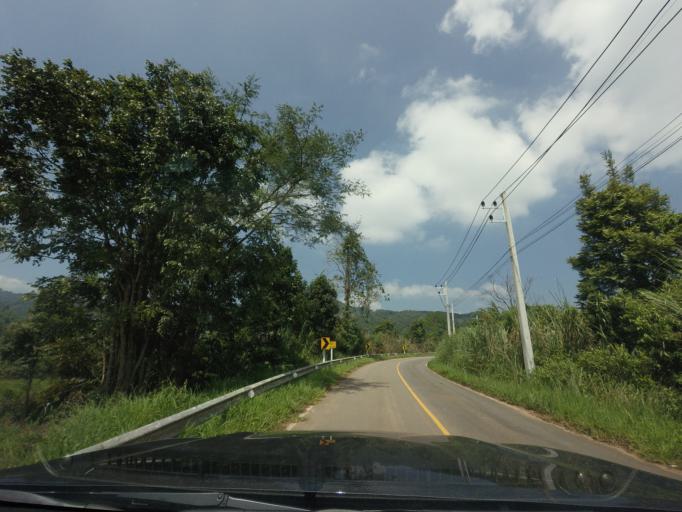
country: TH
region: Loei
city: Na Haeo
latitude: 17.4731
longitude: 100.9193
